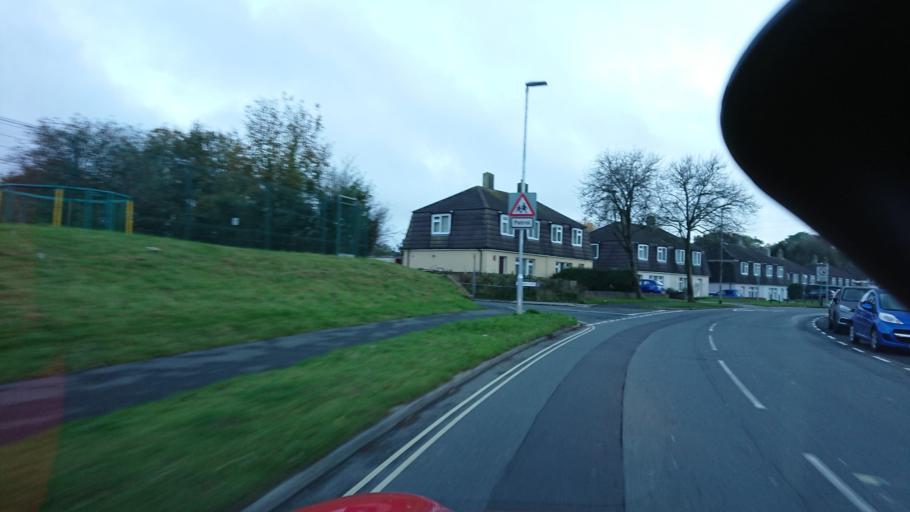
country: GB
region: England
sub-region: Cornwall
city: Torpoint
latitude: 50.4177
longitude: -4.1710
